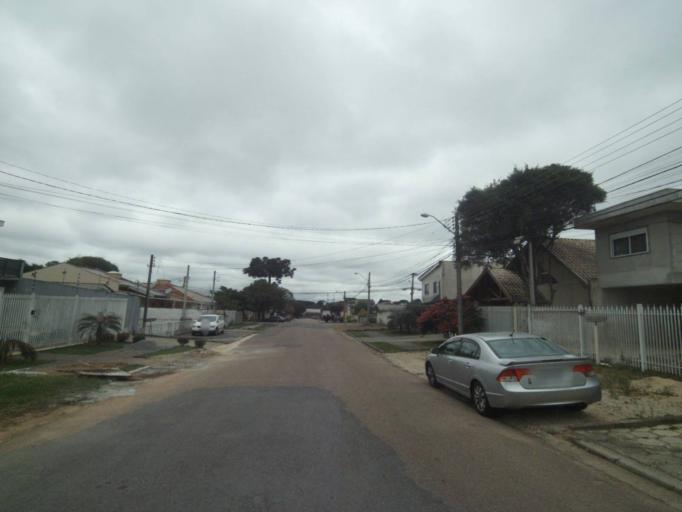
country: BR
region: Parana
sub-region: Sao Jose Dos Pinhais
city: Sao Jose dos Pinhais
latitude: -25.5418
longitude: -49.2805
